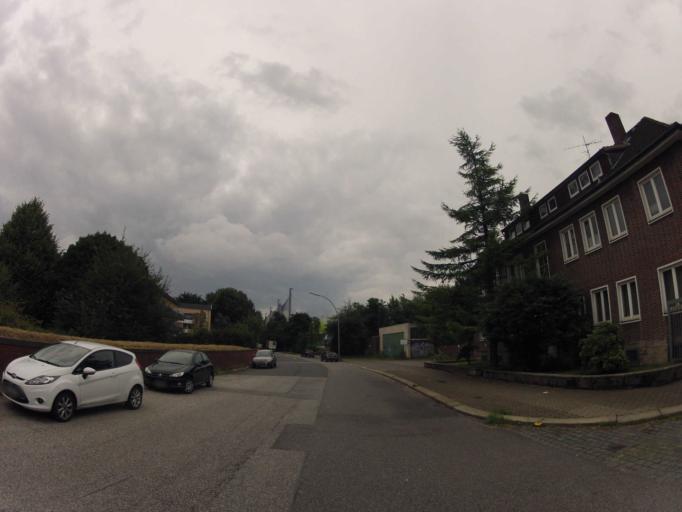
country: DE
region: Hamburg
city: Rothenburgsort
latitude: 53.5346
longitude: 10.0329
